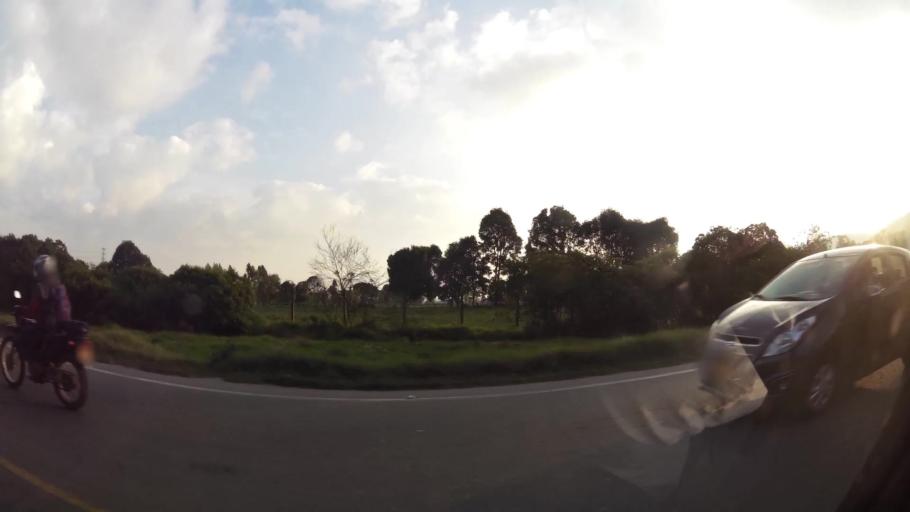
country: CO
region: Cundinamarca
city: Cota
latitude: 4.7981
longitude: -74.1083
